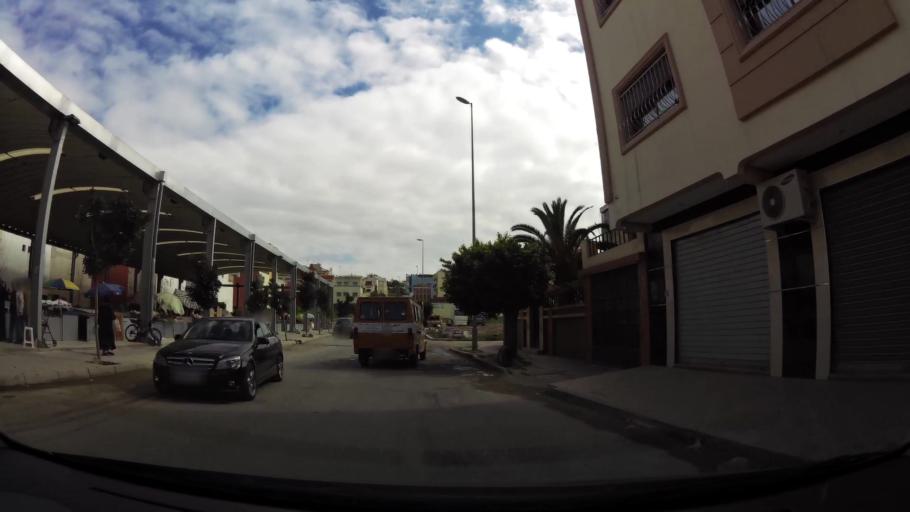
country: MA
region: Tanger-Tetouan
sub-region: Tanger-Assilah
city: Tangier
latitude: 35.7629
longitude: -5.8075
